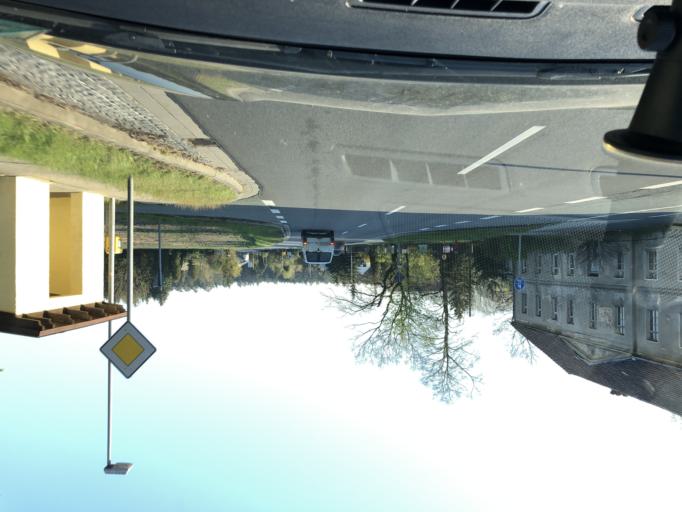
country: DE
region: Saxony
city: Niesky
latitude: 51.3371
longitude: 14.8113
